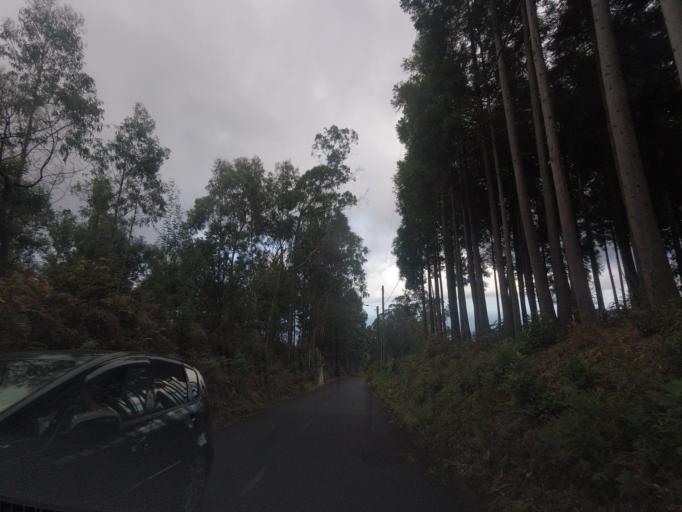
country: PT
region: Madeira
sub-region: Santana
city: Santana
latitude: 32.8001
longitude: -16.8894
